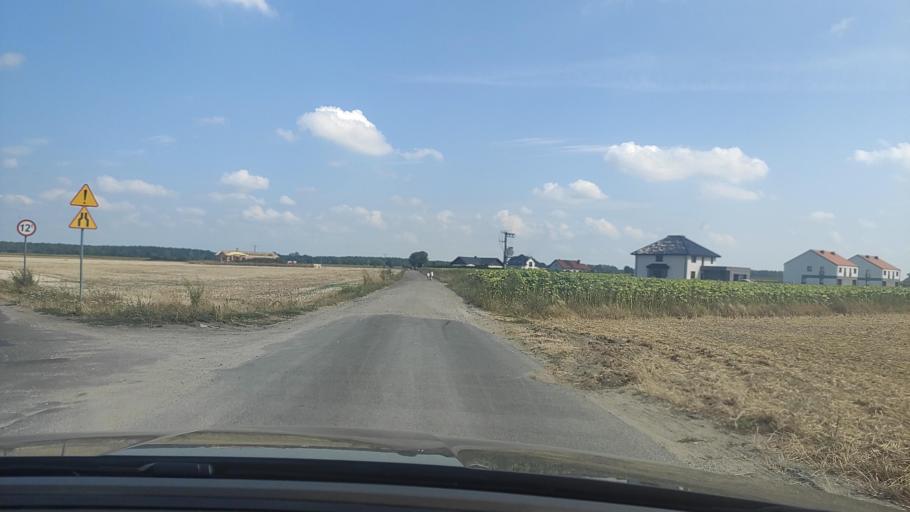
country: PL
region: Greater Poland Voivodeship
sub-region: Powiat poznanski
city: Kostrzyn
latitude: 52.4831
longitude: 17.1912
